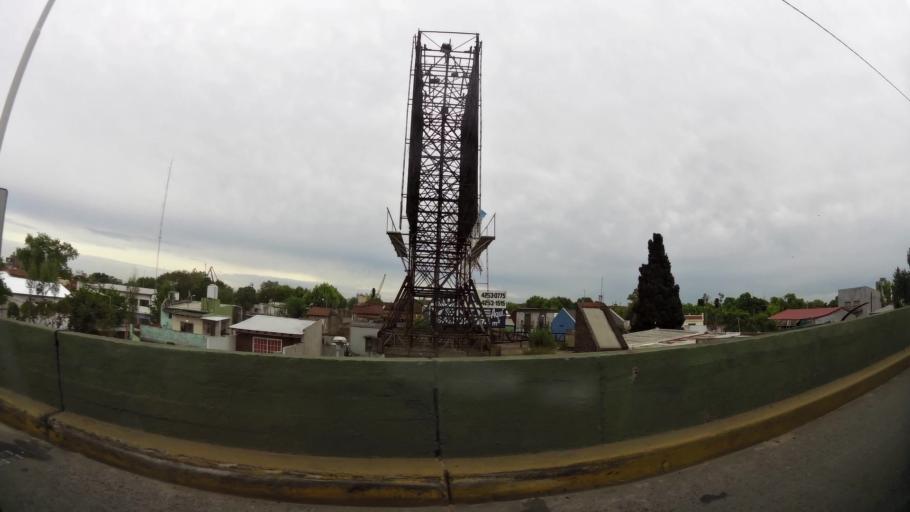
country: AR
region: Buenos Aires
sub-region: Partido de Avellaneda
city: Avellaneda
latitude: -34.6410
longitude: -58.3521
